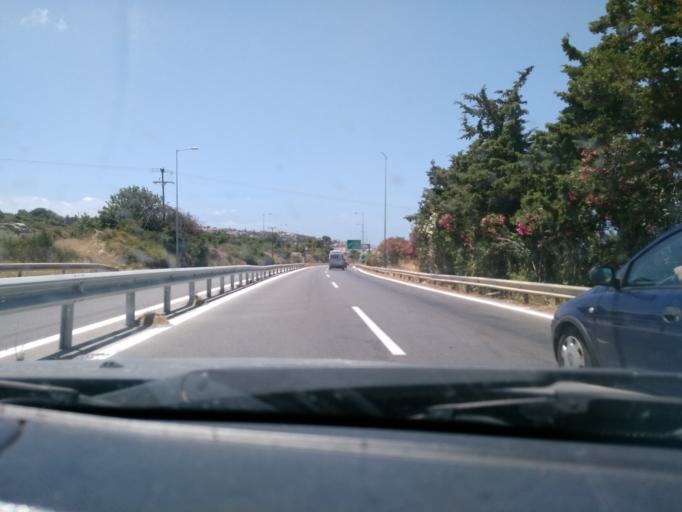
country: GR
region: Crete
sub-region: Nomos Rethymnis
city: Atsipopoulon
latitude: 35.3594
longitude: 24.4517
